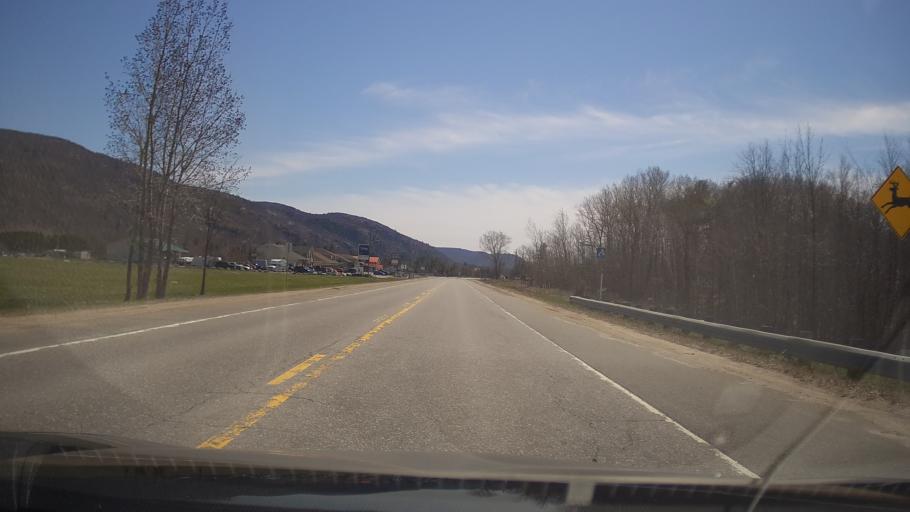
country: CA
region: Quebec
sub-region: Outaouais
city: Wakefield
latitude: 45.5391
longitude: -76.0233
